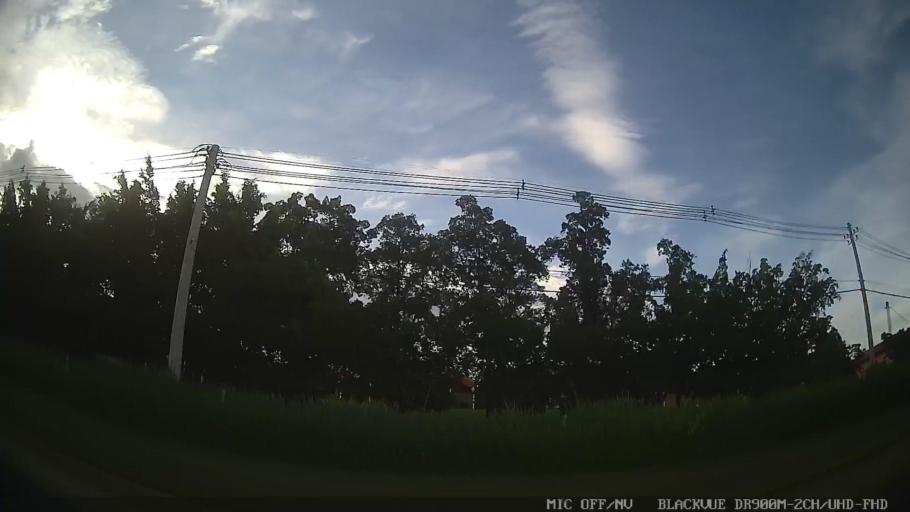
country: BR
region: Sao Paulo
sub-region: Tiete
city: Tiete
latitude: -23.0652
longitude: -47.7291
